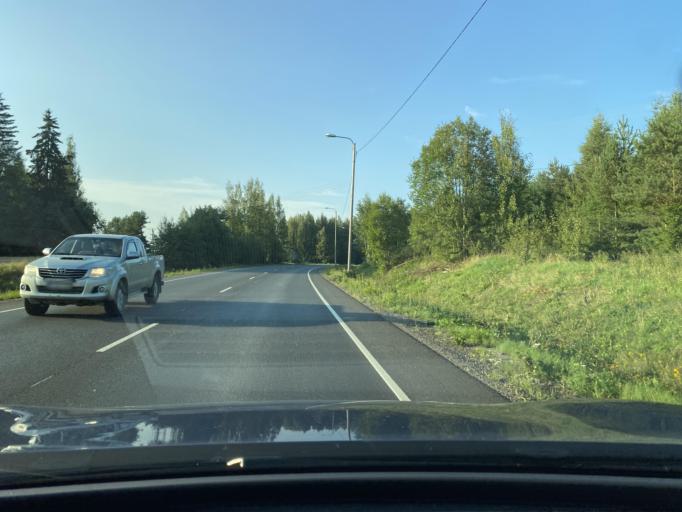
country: FI
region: Kymenlaakso
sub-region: Kouvola
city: Kouvola
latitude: 60.8794
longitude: 26.6016
